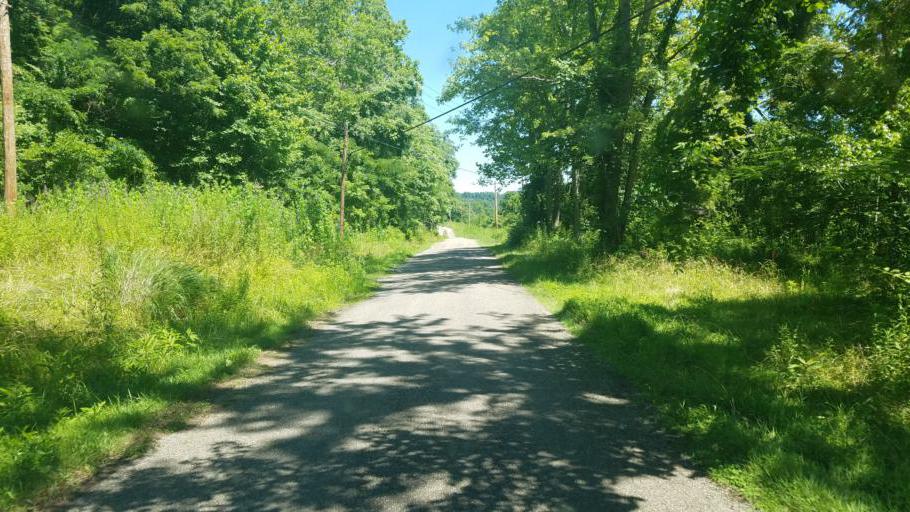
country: US
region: West Virginia
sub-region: Cabell County
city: Lesage
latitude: 38.5687
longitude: -82.2948
